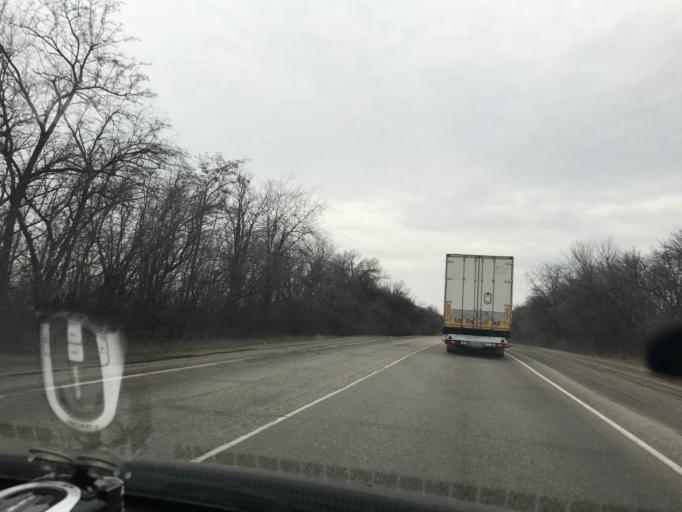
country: RU
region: Krasnodarskiy
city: Mirskoy
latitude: 45.5970
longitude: 40.3968
